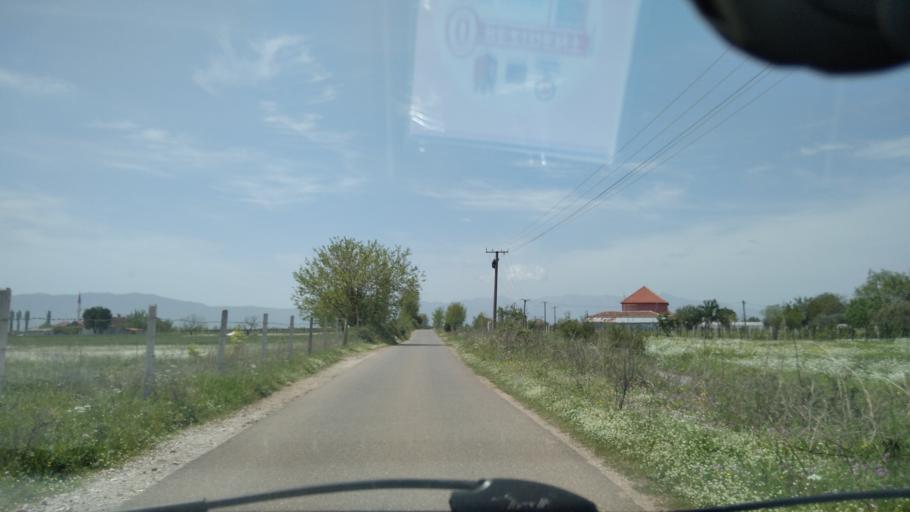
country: AL
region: Shkoder
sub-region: Rrethi i Malesia e Madhe
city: Gruemire
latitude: 42.1451
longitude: 19.5276
